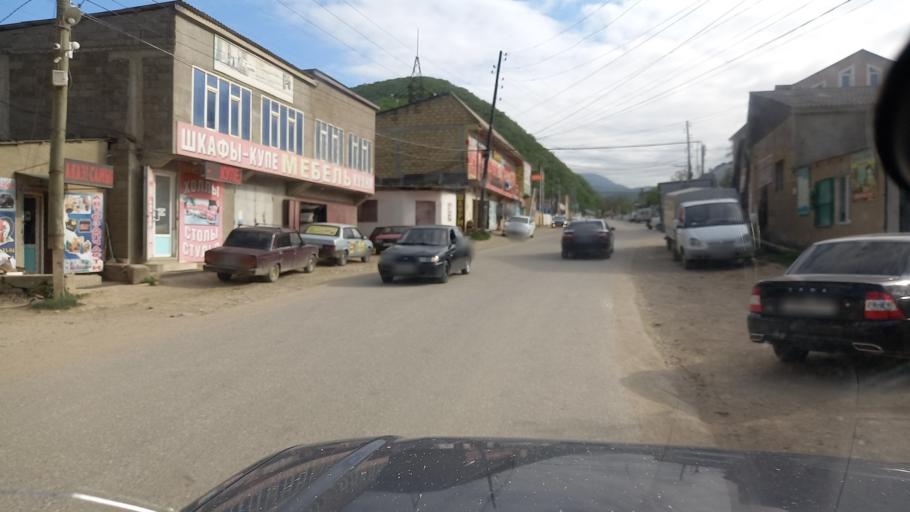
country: RU
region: Dagestan
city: Khuchni
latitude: 41.9616
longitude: 47.9570
